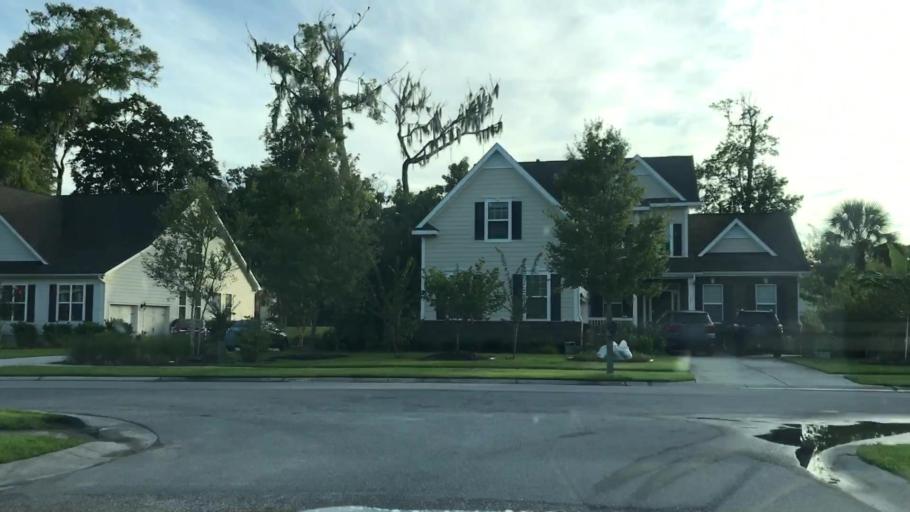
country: US
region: South Carolina
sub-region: Charleston County
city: Shell Point
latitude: 32.8432
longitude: -80.0834
